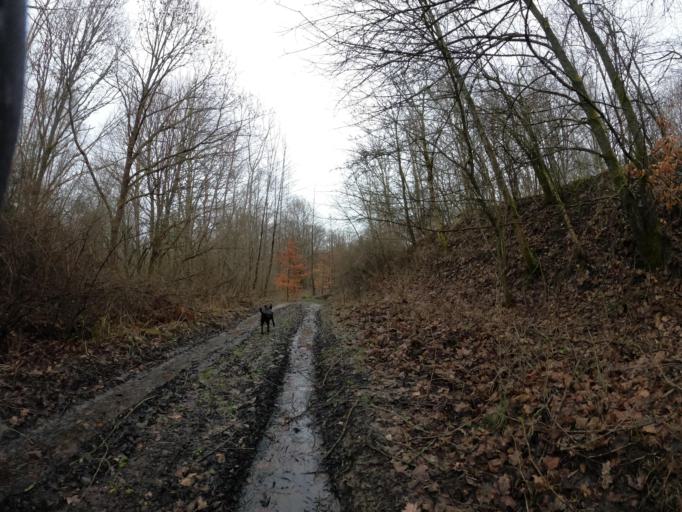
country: PL
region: Greater Poland Voivodeship
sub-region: Powiat zlotowski
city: Sypniewo
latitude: 53.4926
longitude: 16.5622
